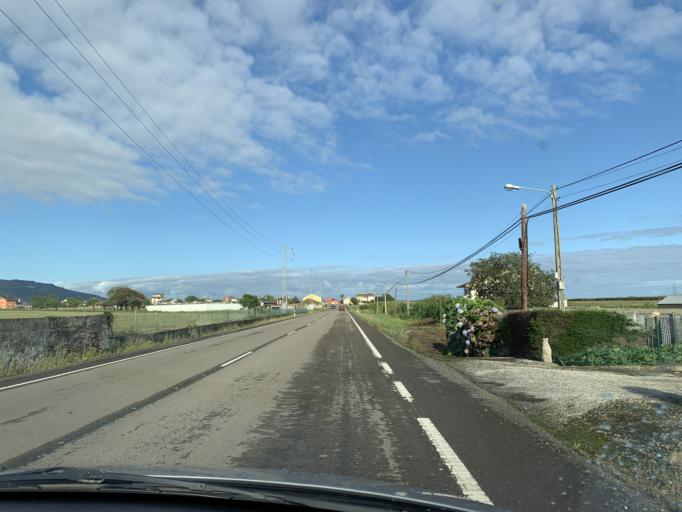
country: ES
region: Galicia
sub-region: Provincia de Lugo
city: Ribadeo
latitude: 43.5446
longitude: -7.0836
